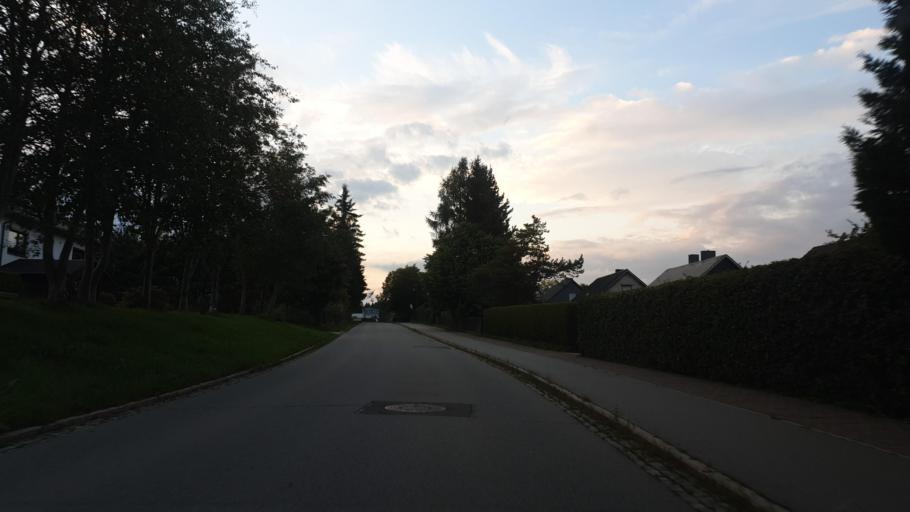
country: DE
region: Saxony
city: Johanngeorgenstadt
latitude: 50.4311
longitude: 12.7182
